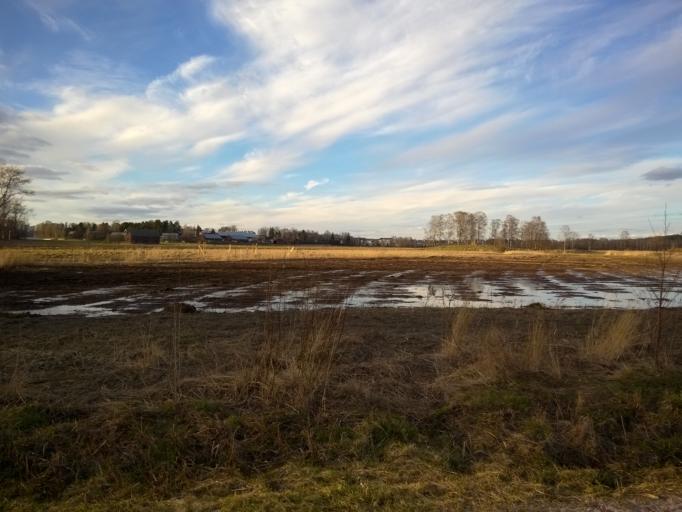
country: FI
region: Uusimaa
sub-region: Helsinki
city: Vantaa
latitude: 60.2146
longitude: 25.0172
